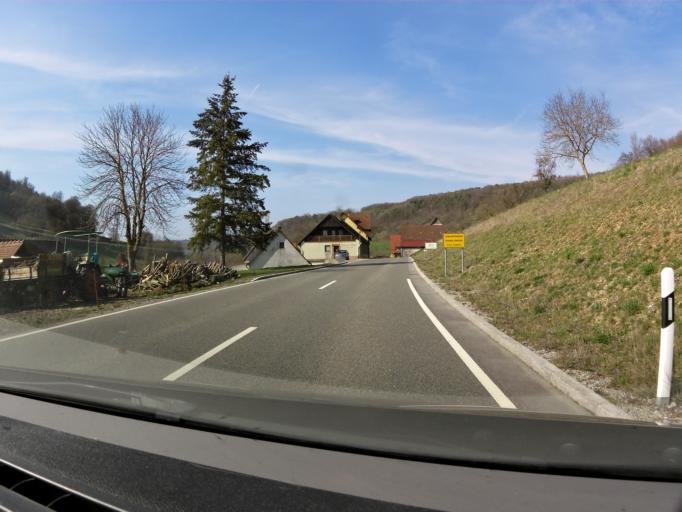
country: DE
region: Bavaria
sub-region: Regierungsbezirk Mittelfranken
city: Adelshofen
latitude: 49.4359
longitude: 10.1405
